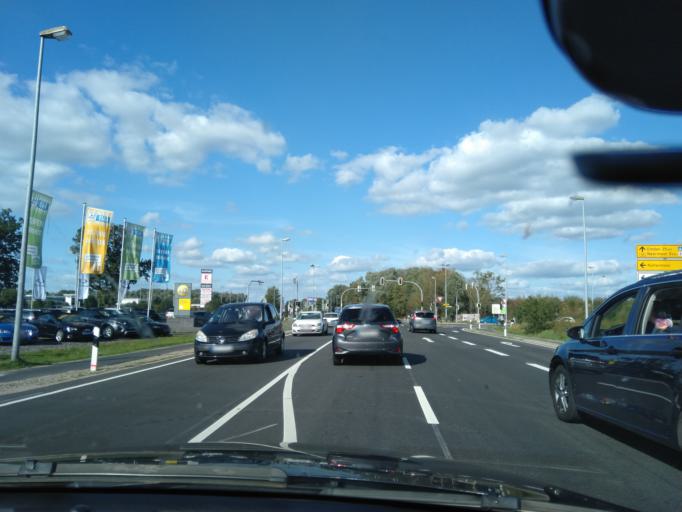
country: DE
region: Lower Saxony
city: Leer
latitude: 53.2582
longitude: 7.4592
